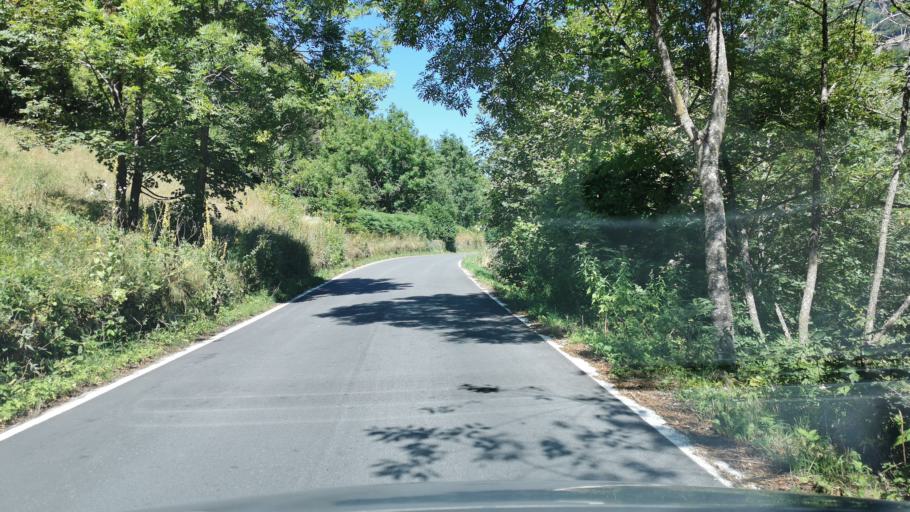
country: IT
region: Piedmont
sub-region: Provincia di Cuneo
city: Demonte
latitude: 44.2287
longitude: 7.3080
